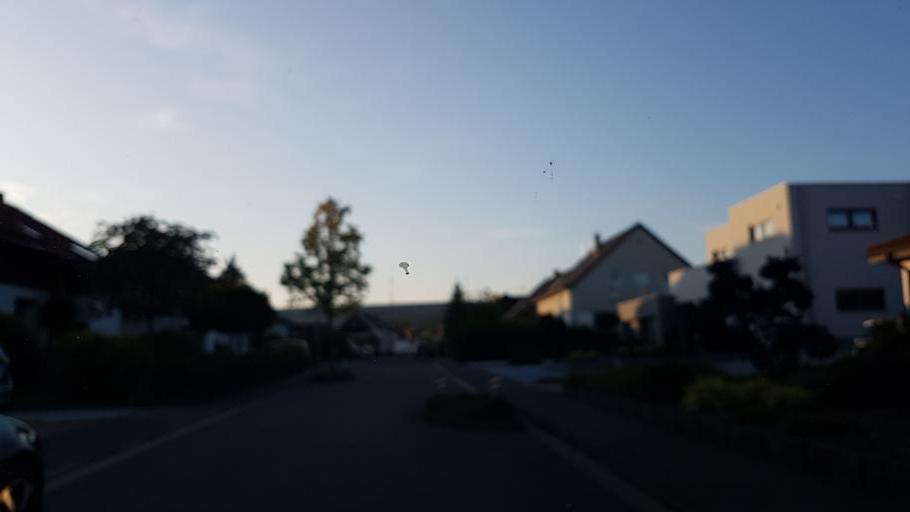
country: DE
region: Saarland
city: Weiskirchen
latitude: 49.5513
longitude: 6.8201
